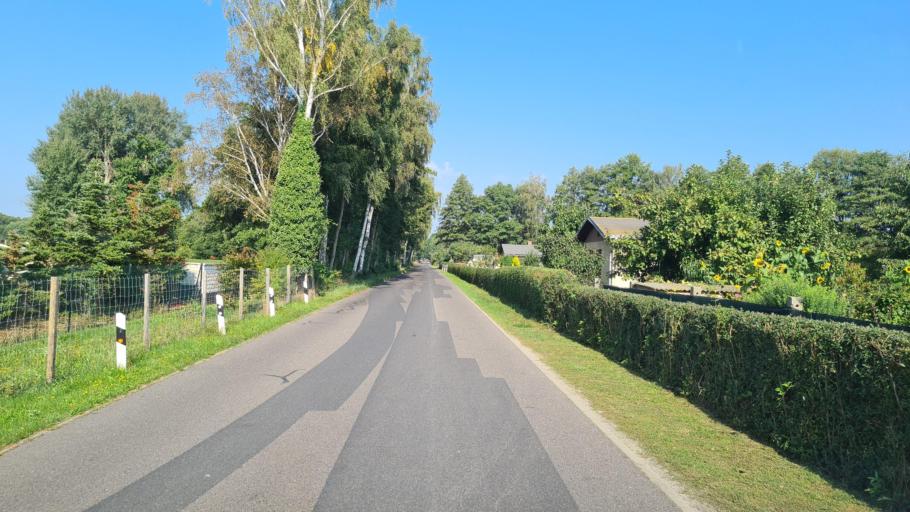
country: DE
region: Brandenburg
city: Kolkwitz
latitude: 51.7395
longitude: 14.2488
